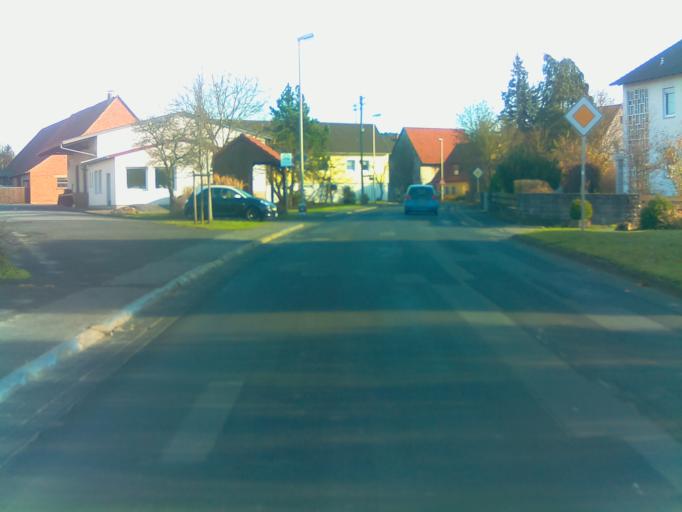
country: DE
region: Bavaria
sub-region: Regierungsbezirk Unterfranken
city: Roden
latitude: 49.8957
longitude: 9.6226
